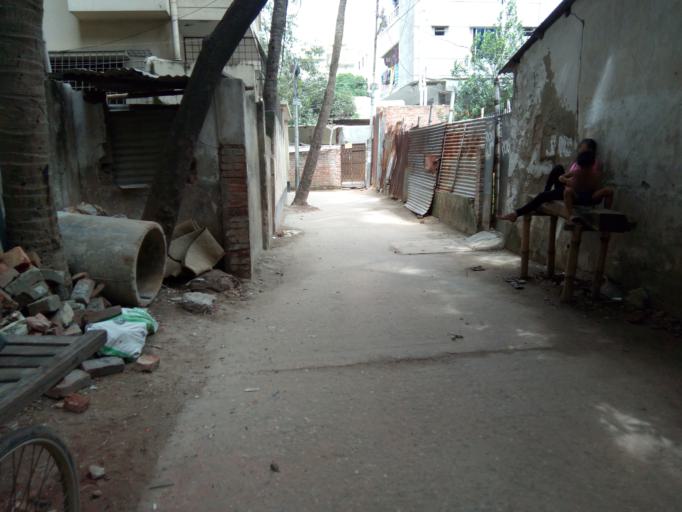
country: BD
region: Dhaka
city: Azimpur
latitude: 23.7485
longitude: 90.3655
